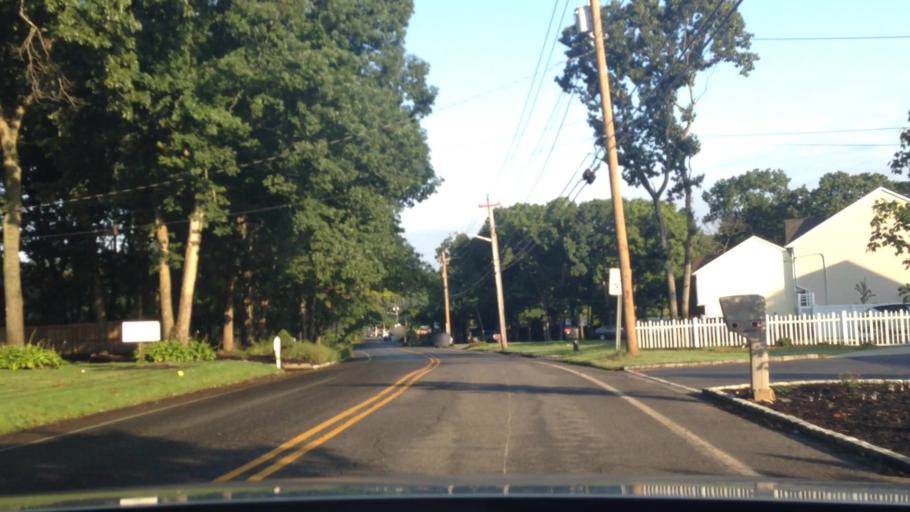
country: US
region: New York
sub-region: Suffolk County
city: Centereach
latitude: 40.8539
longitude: -73.0712
